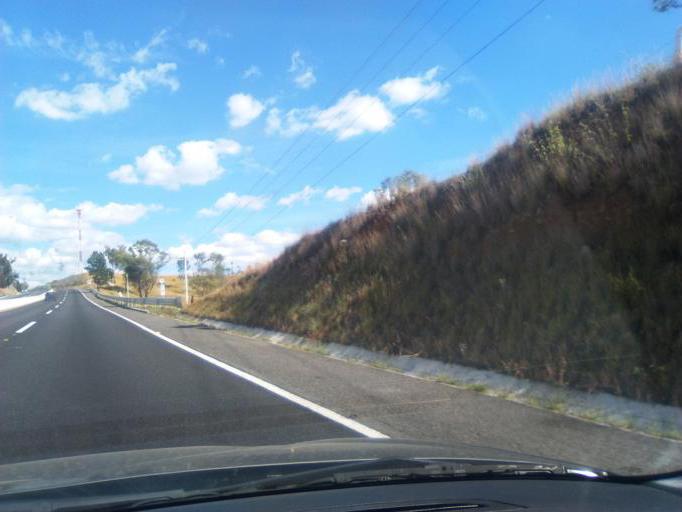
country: MX
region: Guanajuato
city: Santa Teresa
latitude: 20.9645
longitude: -101.3325
